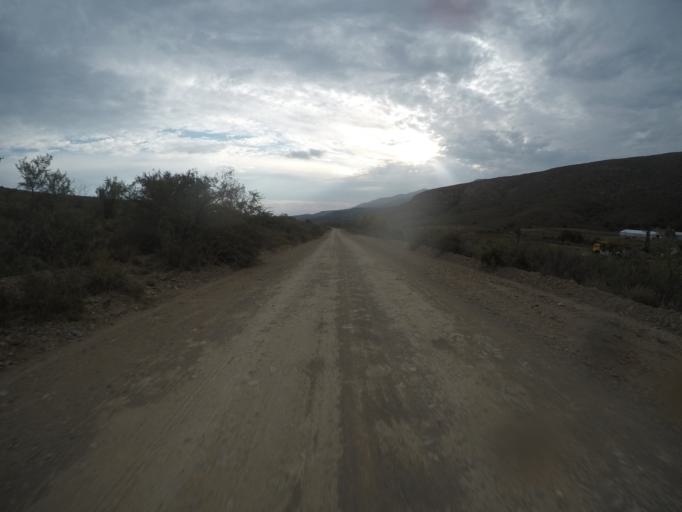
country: ZA
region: Eastern Cape
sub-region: Cacadu District Municipality
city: Willowmore
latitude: -33.4866
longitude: 23.5481
